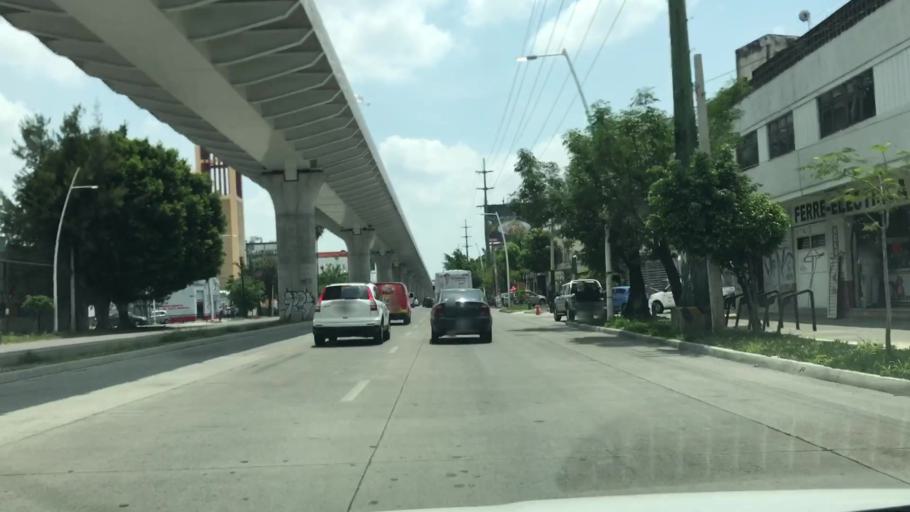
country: MX
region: Jalisco
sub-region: Zapopan
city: Zapopan
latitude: 20.7039
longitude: -103.3621
